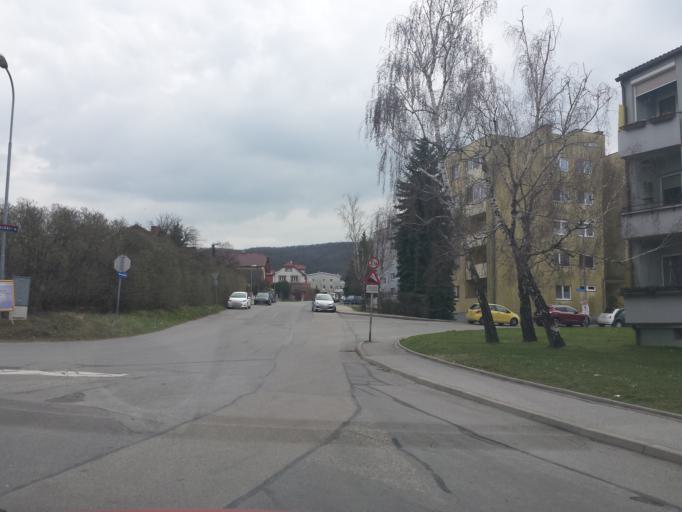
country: AT
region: Lower Austria
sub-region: Politischer Bezirk Bruck an der Leitha
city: Hainburg an der Donau
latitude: 48.1420
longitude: 16.9543
